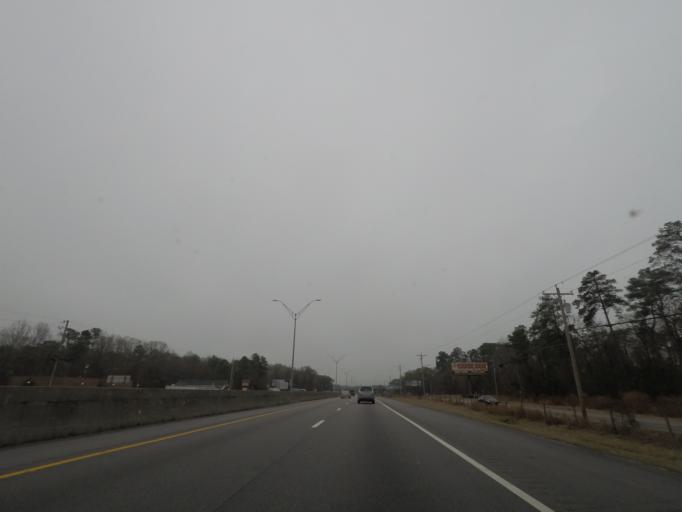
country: US
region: North Carolina
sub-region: Robeson County
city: Lumberton
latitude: 34.6552
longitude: -79.0108
